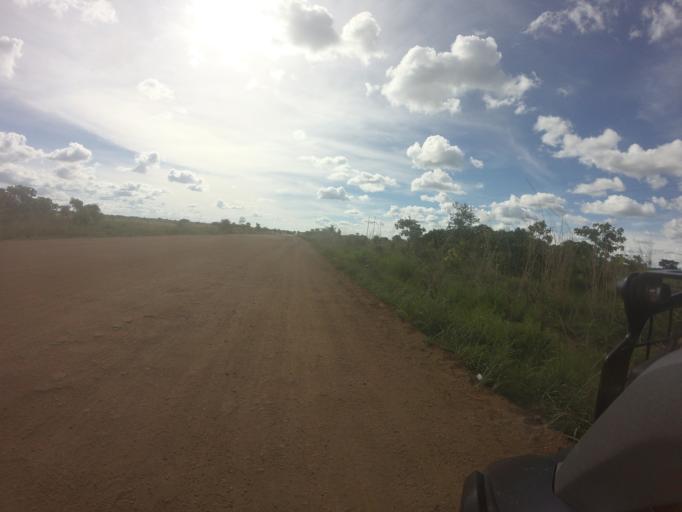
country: ZM
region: Western
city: Kaoma
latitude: -14.8825
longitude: 25.3432
